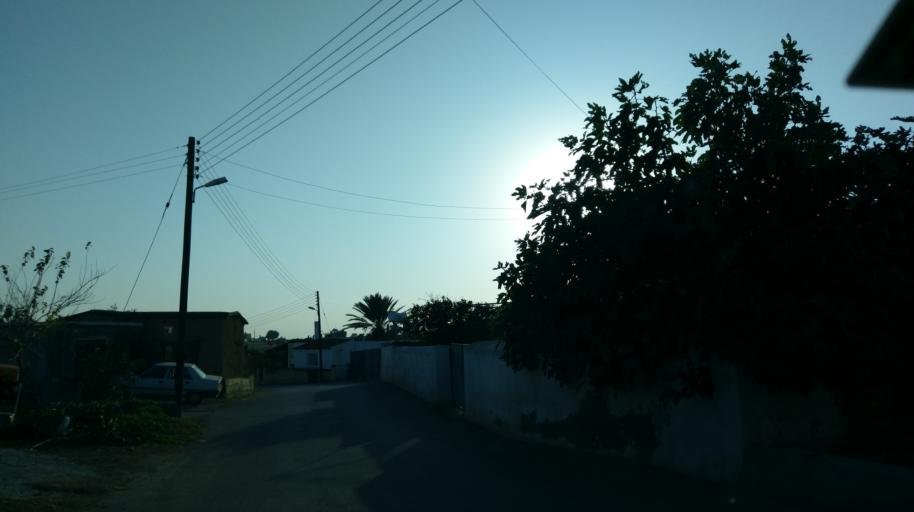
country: CY
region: Ammochostos
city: Trikomo
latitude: 35.3948
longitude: 33.9725
